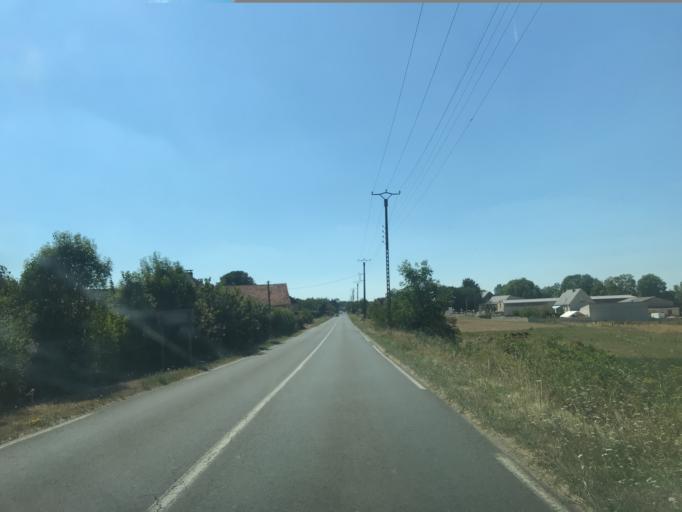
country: FR
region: Aquitaine
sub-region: Departement de la Dordogne
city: Eyvigues-et-Eybenes
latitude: 44.9740
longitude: 1.3123
